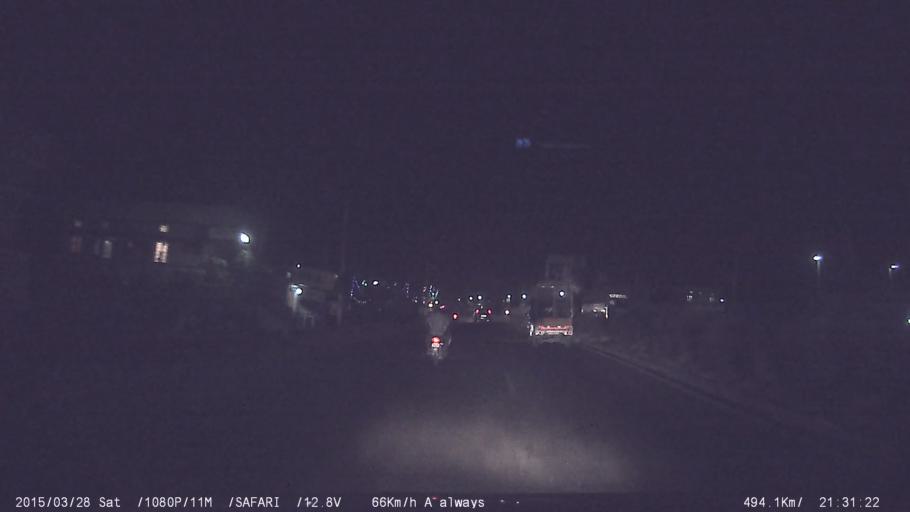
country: IN
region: Karnataka
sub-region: Ramanagara
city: Ramanagaram
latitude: 12.8425
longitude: 77.4206
